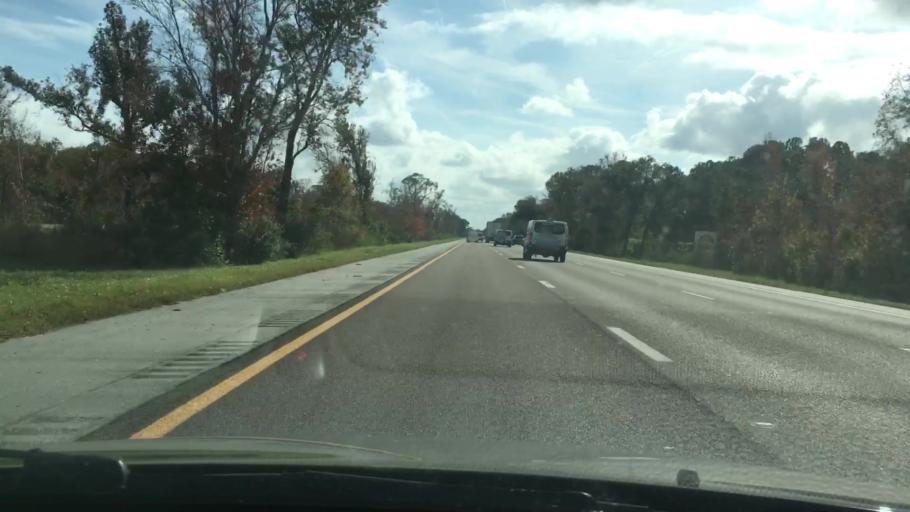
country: US
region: Florida
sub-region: Volusia County
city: Oak Hill
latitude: 28.8879
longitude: -80.9265
